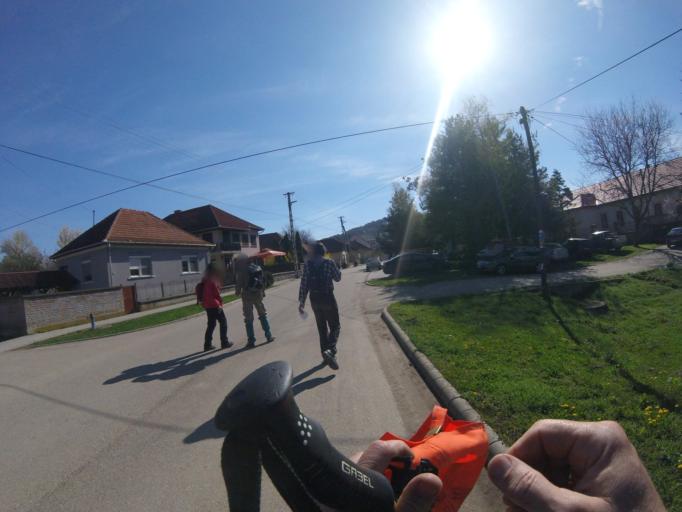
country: HU
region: Borsod-Abauj-Zemplen
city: Szendro
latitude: 48.4092
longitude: 20.7252
